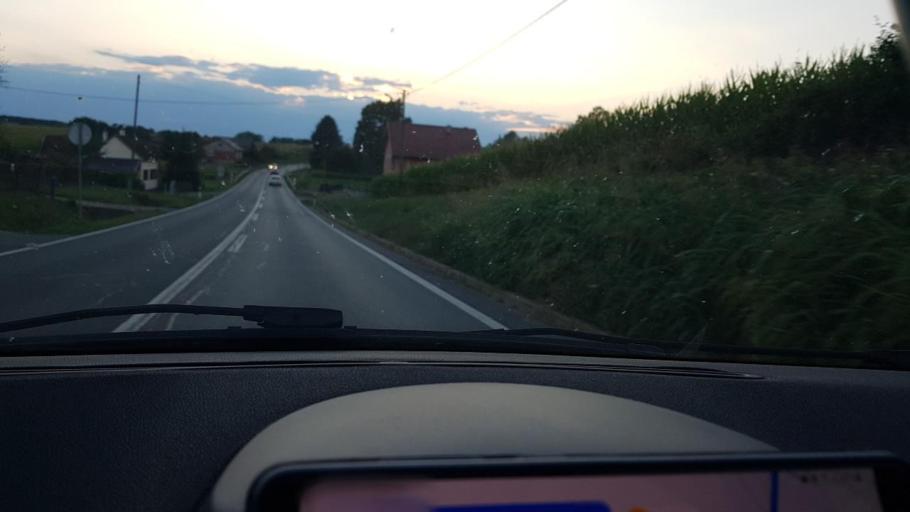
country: HR
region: Bjelovarsko-Bilogorska
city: Zdralovi
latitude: 45.8677
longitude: 16.9087
